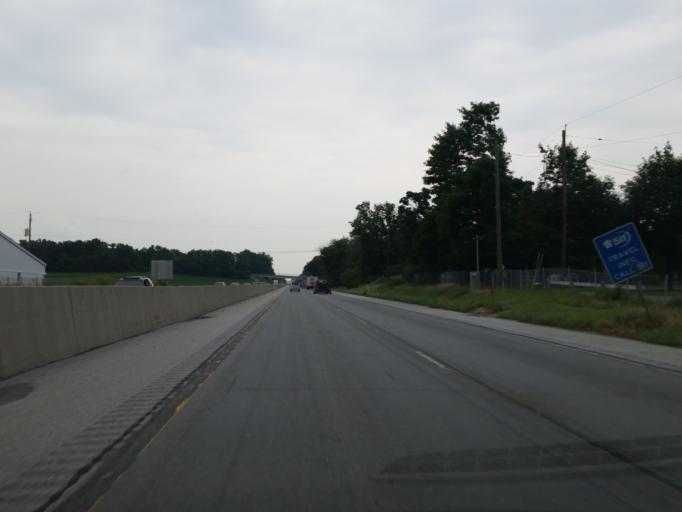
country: US
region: Pennsylvania
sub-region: York County
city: North York
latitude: 40.0004
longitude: -76.7369
